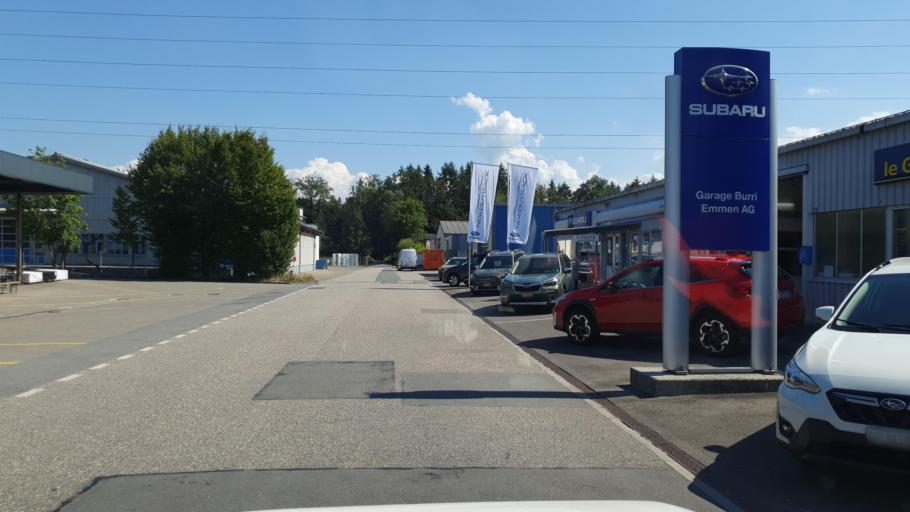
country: CH
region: Lucerne
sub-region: Lucerne-Land District
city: Buchrain
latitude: 47.1084
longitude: 8.3242
